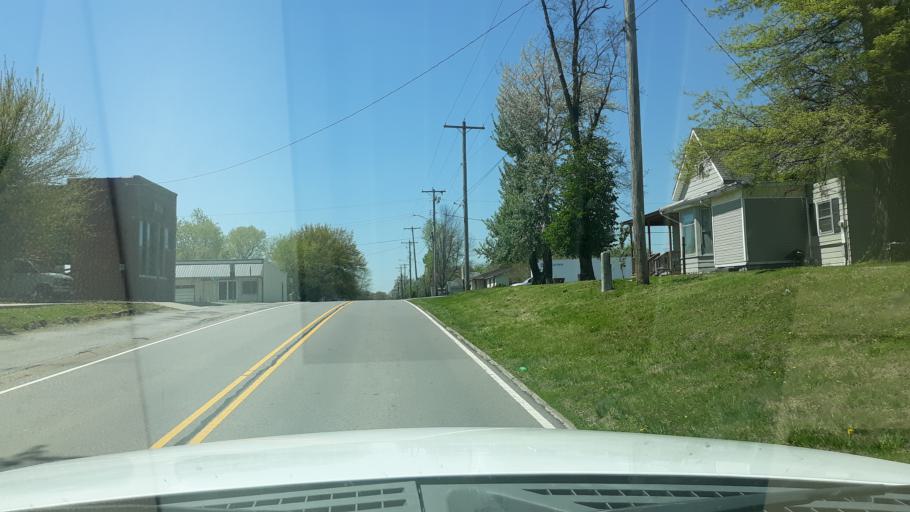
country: US
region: Illinois
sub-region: Saline County
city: Harrisburg
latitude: 37.8268
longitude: -88.5324
